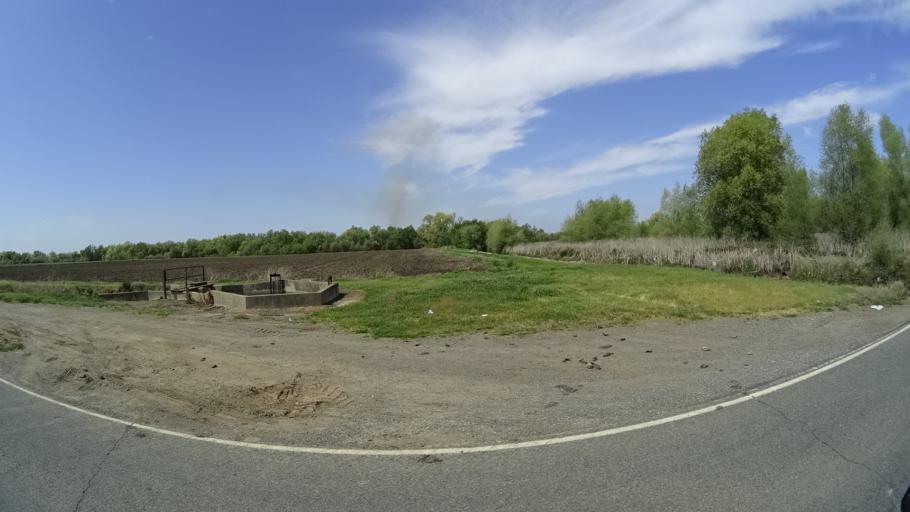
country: US
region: California
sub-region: Butte County
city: Durham
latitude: 39.5217
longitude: -121.8569
